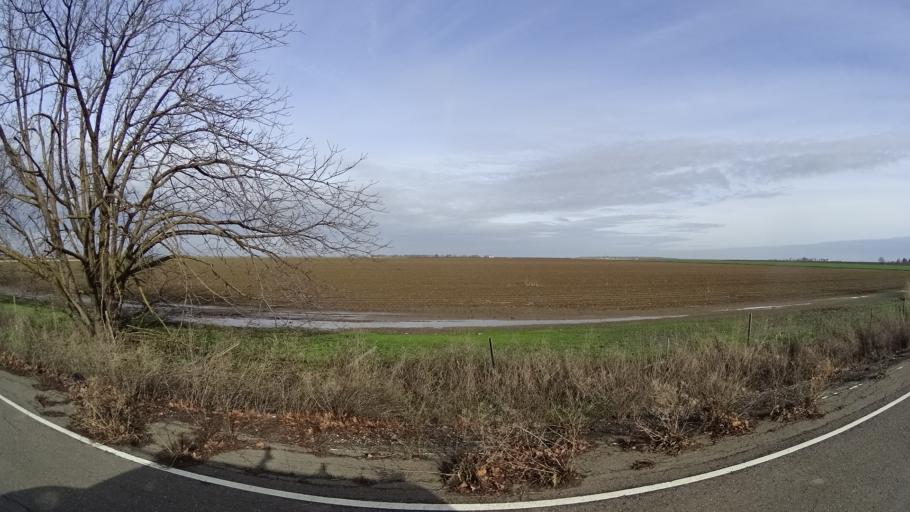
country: US
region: California
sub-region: Yolo County
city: Davis
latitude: 38.5651
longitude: -121.7003
